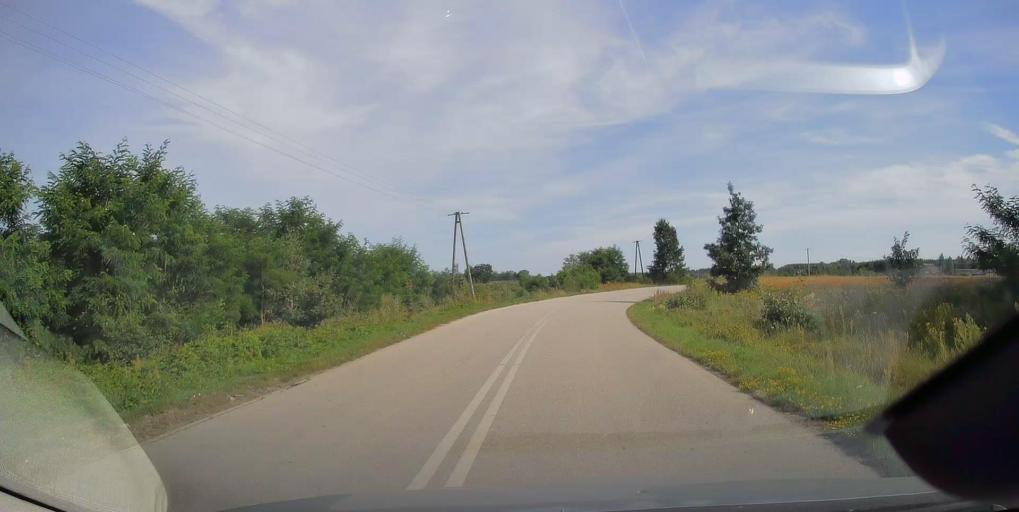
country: PL
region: Lodz Voivodeship
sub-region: Powiat opoczynski
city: Mniszkow
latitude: 51.3521
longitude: 20.0396
